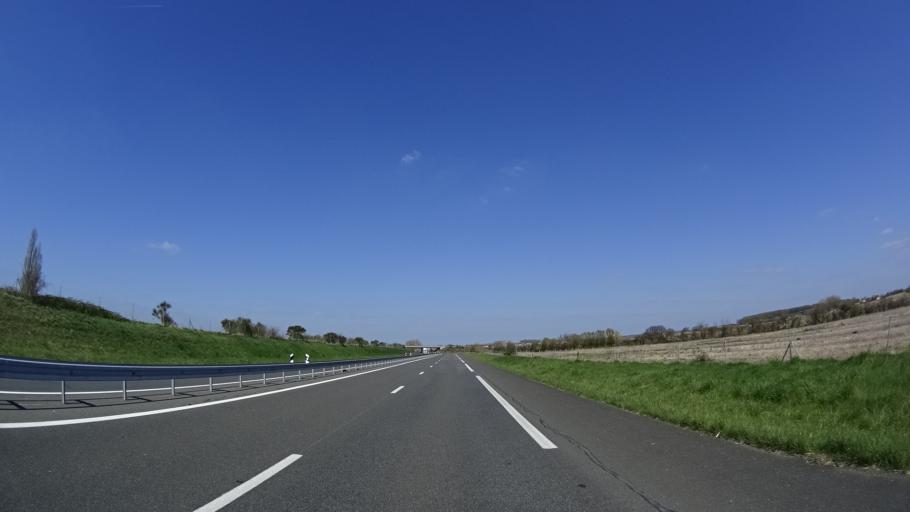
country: FR
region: Pays de la Loire
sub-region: Departement de Maine-et-Loire
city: Saint-Jean
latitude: 47.2688
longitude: -0.3355
